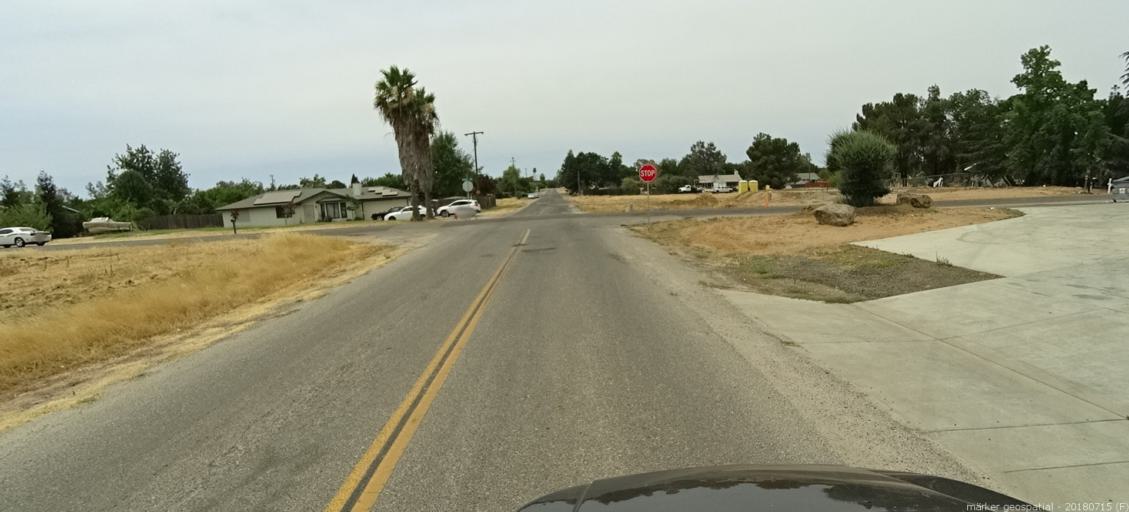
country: US
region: California
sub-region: Madera County
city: Madera Acres
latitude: 36.9991
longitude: -120.0763
